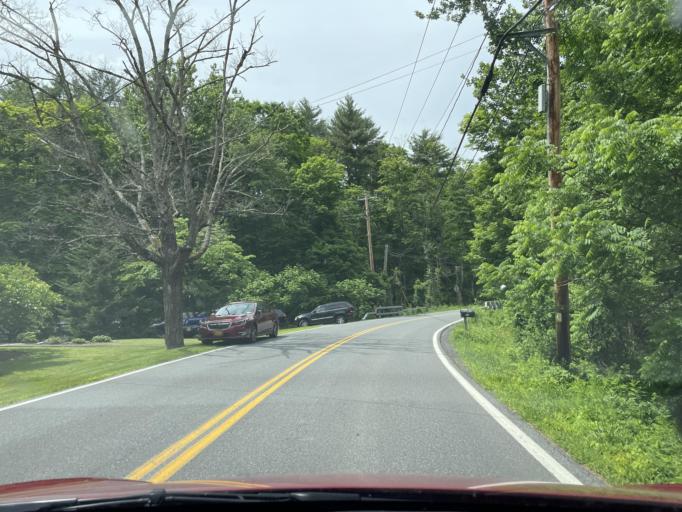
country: US
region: New York
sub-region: Ulster County
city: Zena
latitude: 42.0185
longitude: -74.0781
